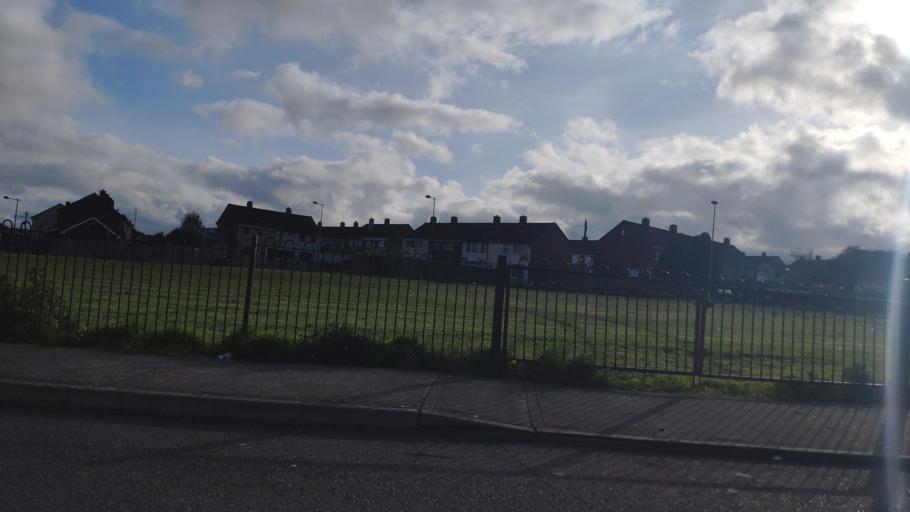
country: IE
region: Munster
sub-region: County Cork
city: Cork
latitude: 51.9102
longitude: -8.4901
